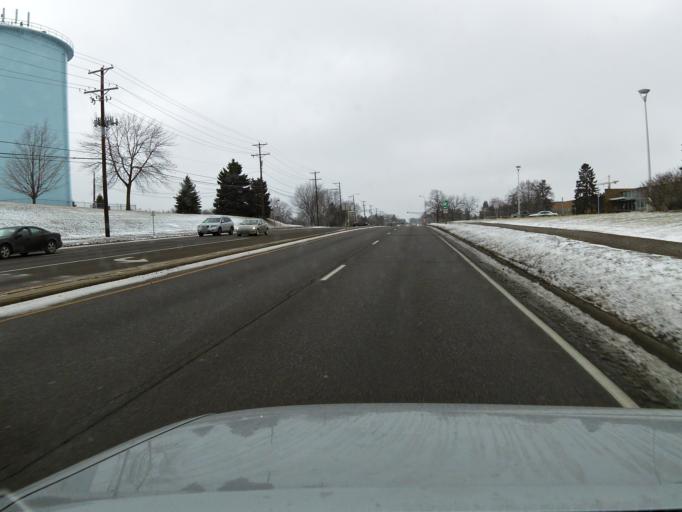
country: US
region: Minnesota
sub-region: Ramsey County
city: Maplewood
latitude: 44.9523
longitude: -93.0048
